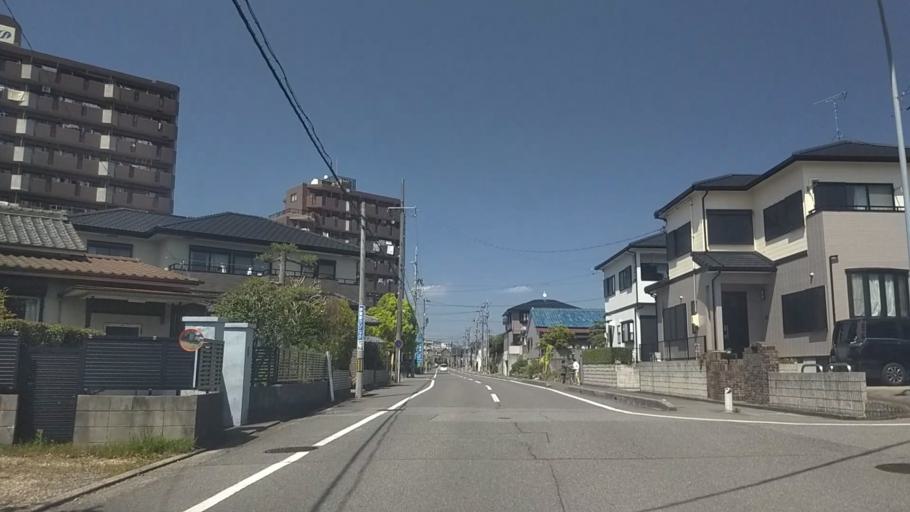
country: JP
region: Aichi
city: Okazaki
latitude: 34.9735
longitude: 137.1708
